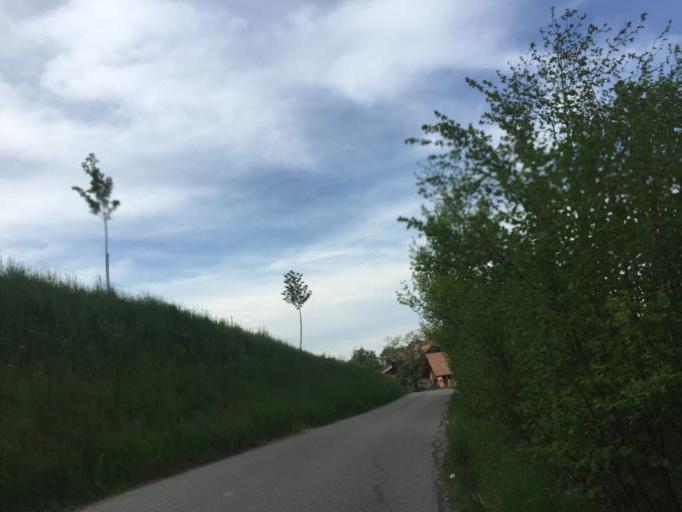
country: CH
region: Bern
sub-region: Bern-Mittelland District
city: Munsingen
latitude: 46.8566
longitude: 7.5475
